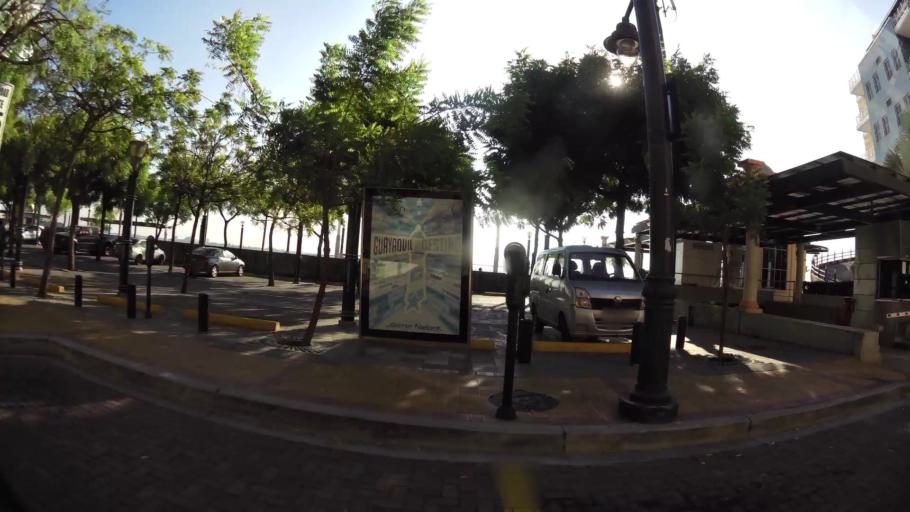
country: EC
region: Guayas
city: Eloy Alfaro
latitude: -2.1804
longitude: -79.8745
